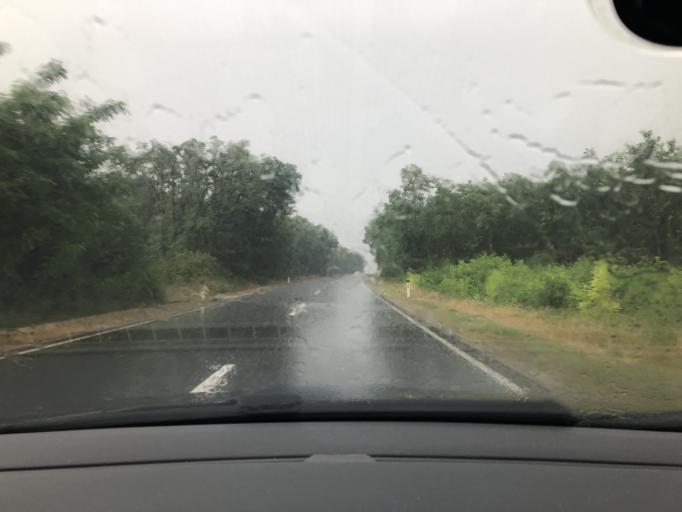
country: AT
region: Lower Austria
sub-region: Politischer Bezirk Ganserndorf
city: Marchegg
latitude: 48.2268
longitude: 16.9024
